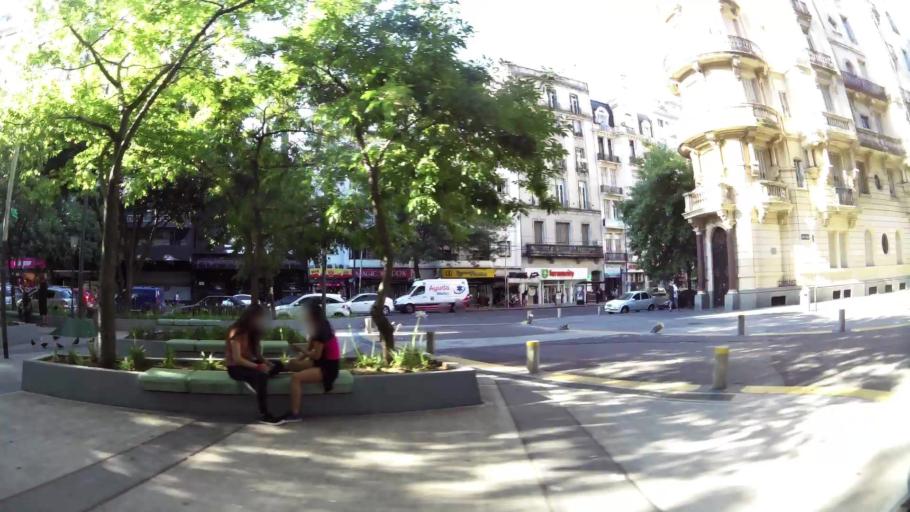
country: AR
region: Buenos Aires F.D.
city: Colegiales
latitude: -34.6151
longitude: -58.4285
